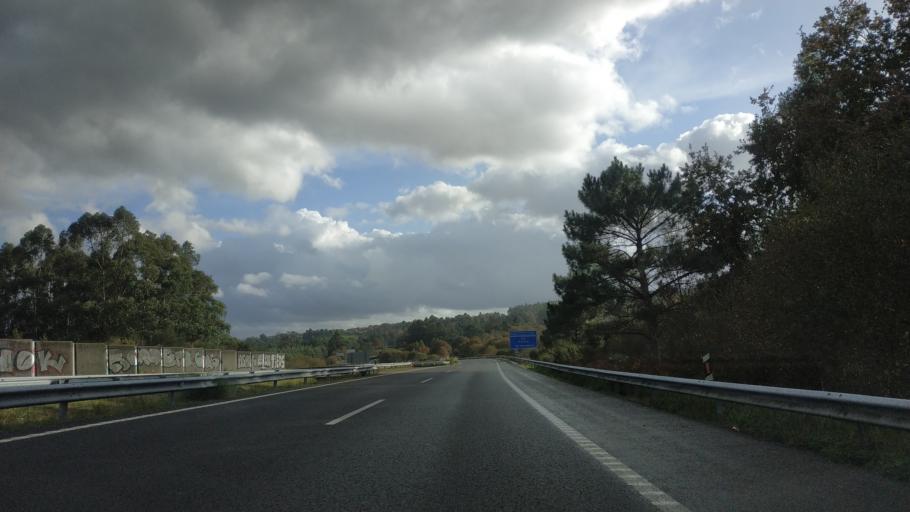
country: ES
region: Galicia
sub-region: Provincia da Coruna
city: Cambre
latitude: 43.2720
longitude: -8.3608
